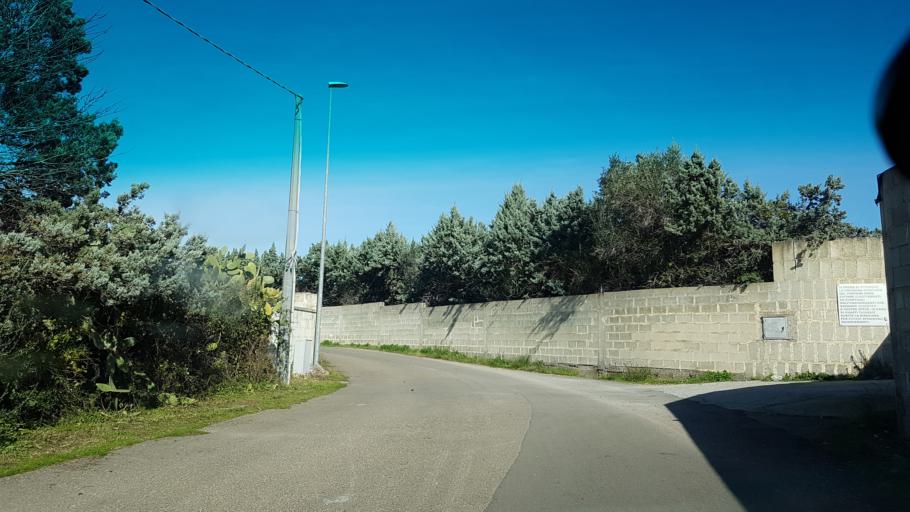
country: IT
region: Apulia
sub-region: Provincia di Lecce
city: Arnesano
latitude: 40.3589
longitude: 18.1060
